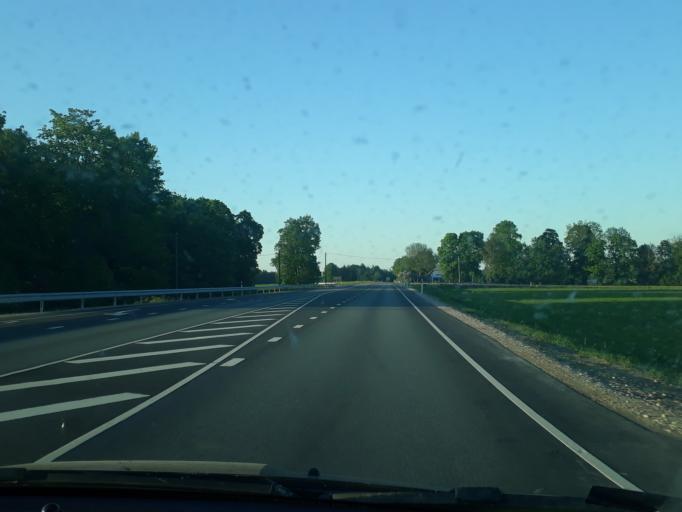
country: EE
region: Paernumaa
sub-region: Tootsi vald
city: Tootsi
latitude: 58.5520
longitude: 24.8522
